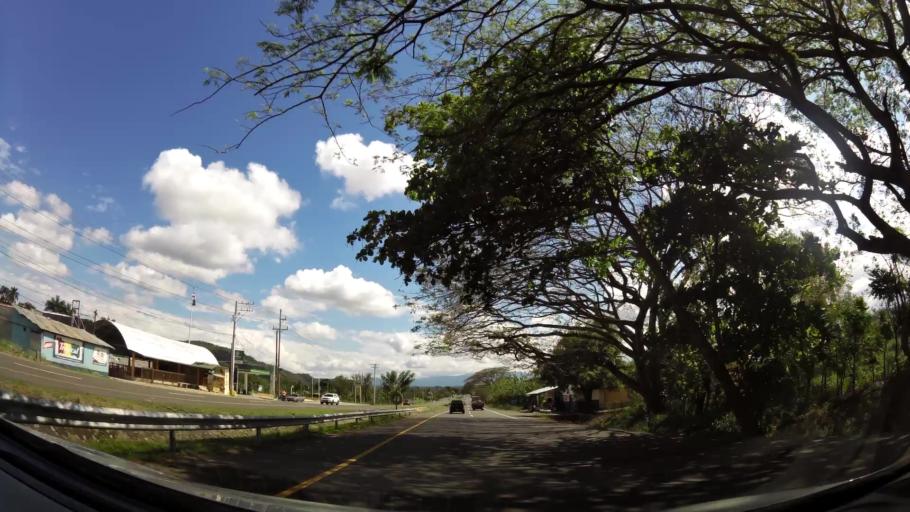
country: DO
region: La Vega
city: Rio Verde Arriba
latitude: 19.3207
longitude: -70.5874
